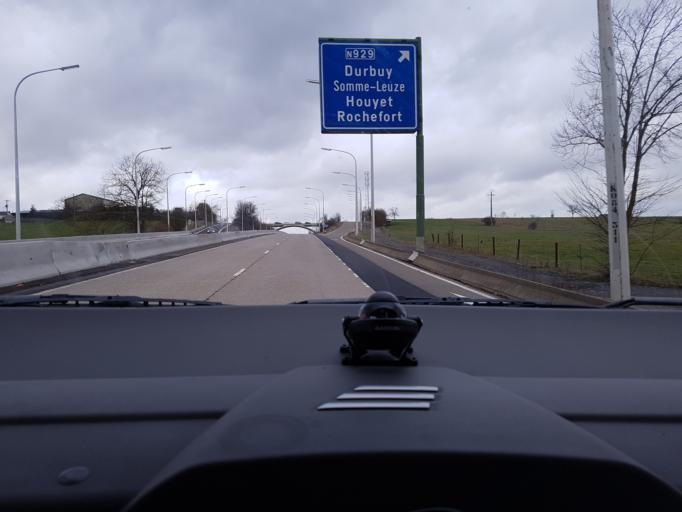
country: BE
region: Wallonia
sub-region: Province de Namur
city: Hamois
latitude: 50.2733
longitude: 5.2390
